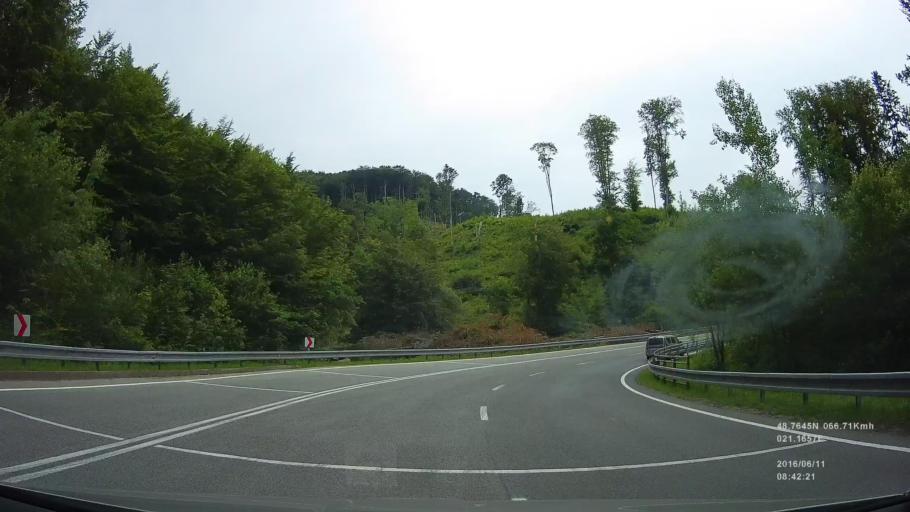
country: SK
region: Kosicky
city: Kosice
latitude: 48.7501
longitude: 21.2282
